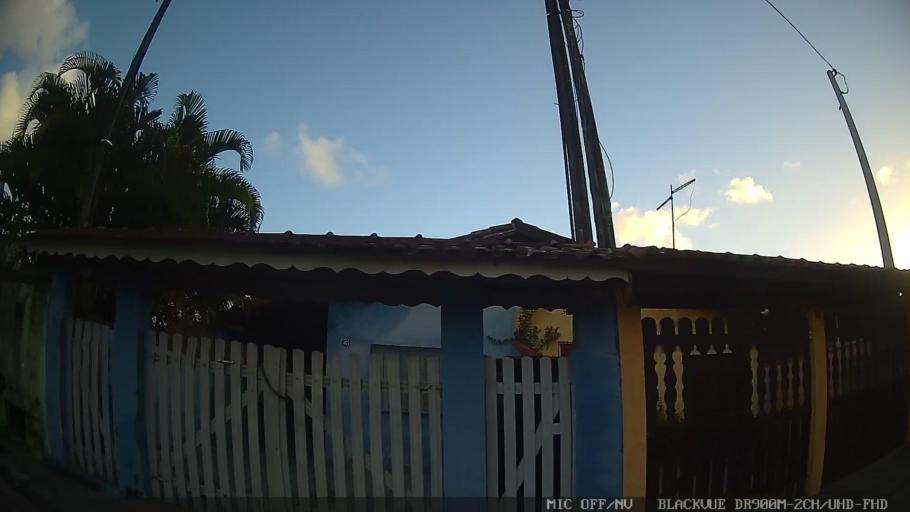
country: BR
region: Sao Paulo
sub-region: Itanhaem
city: Itanhaem
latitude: -24.1462
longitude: -46.7271
